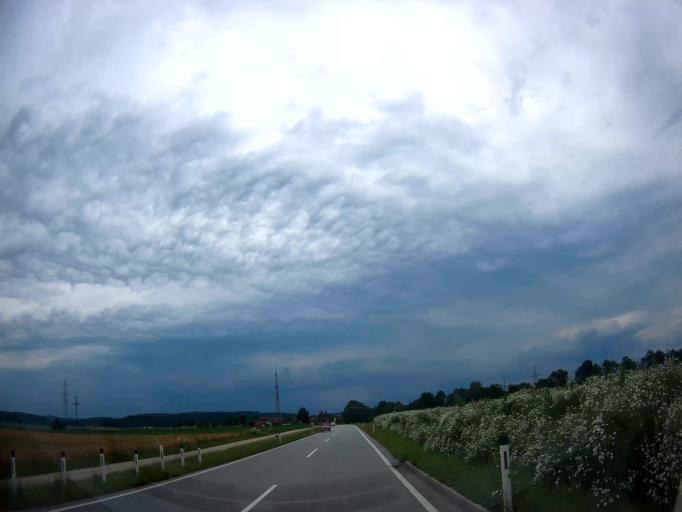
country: AT
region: Upper Austria
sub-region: Politischer Bezirk Braunau am Inn
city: Altheim
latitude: 48.2457
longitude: 13.1917
